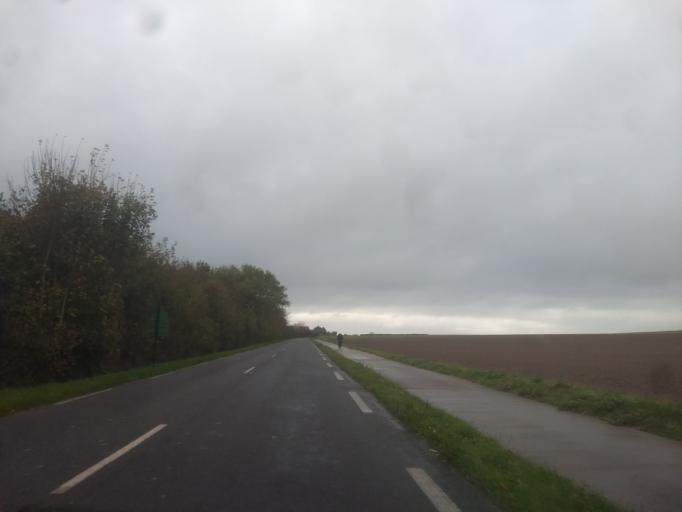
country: FR
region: Nord-Pas-de-Calais
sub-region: Departement du Pas-de-Calais
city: Wissant
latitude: 50.8973
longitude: 1.6850
